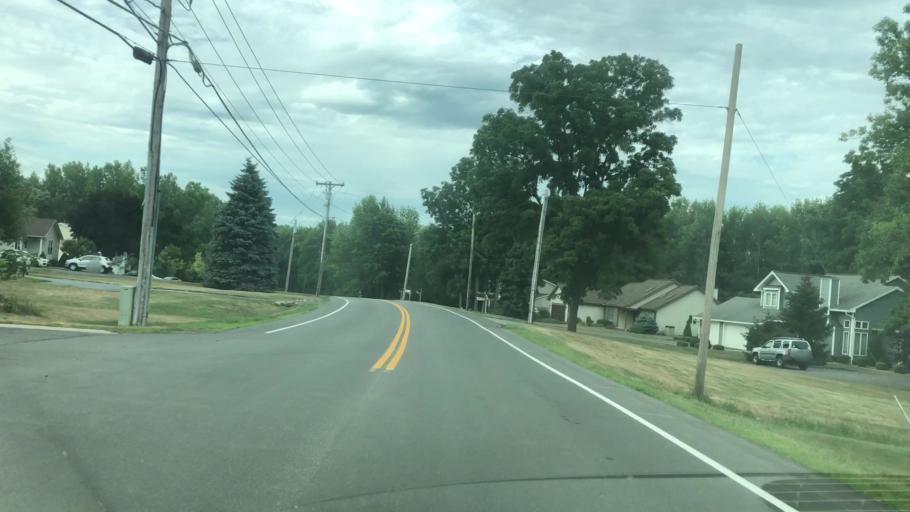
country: US
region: New York
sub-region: Wayne County
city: Macedon
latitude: 43.1320
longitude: -77.3530
